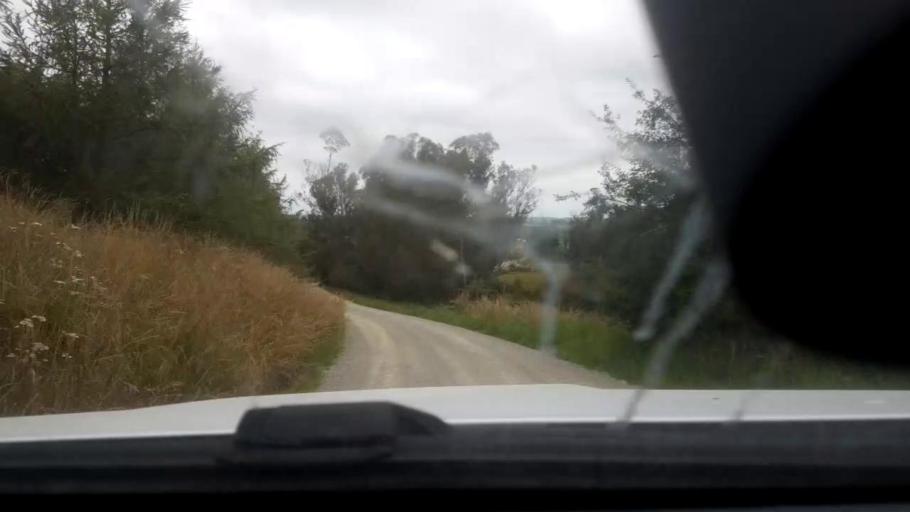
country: NZ
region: Canterbury
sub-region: Timaru District
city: Pleasant Point
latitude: -44.2142
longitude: 171.1799
